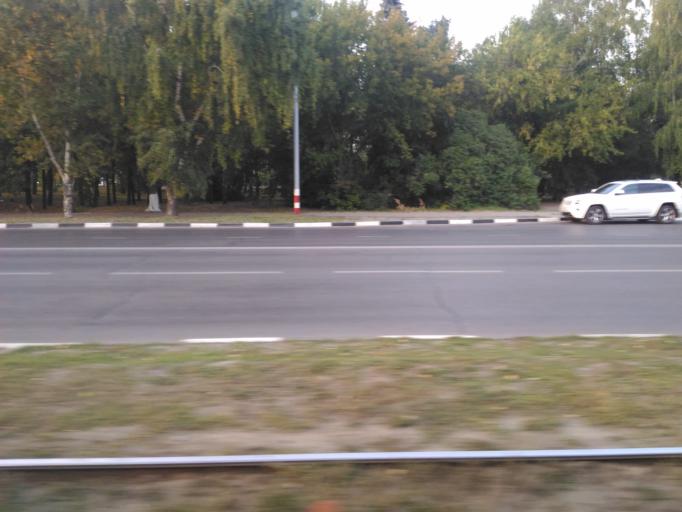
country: RU
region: Ulyanovsk
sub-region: Ulyanovskiy Rayon
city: Ulyanovsk
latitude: 54.3078
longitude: 48.3381
